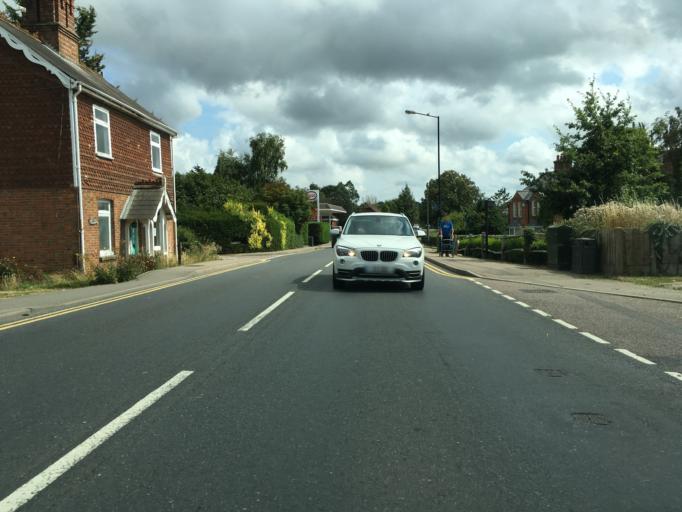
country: GB
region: England
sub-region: Kent
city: Tenterden
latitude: 51.0845
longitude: 0.6919
